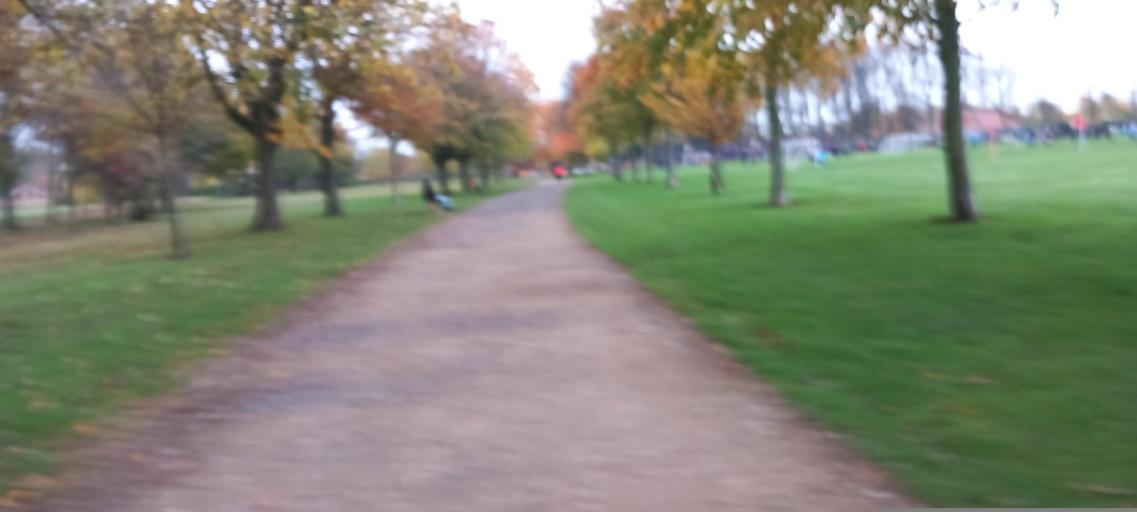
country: GB
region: England
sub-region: East Riding of Yorkshire
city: Airmyn
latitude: 53.7118
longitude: -0.8943
